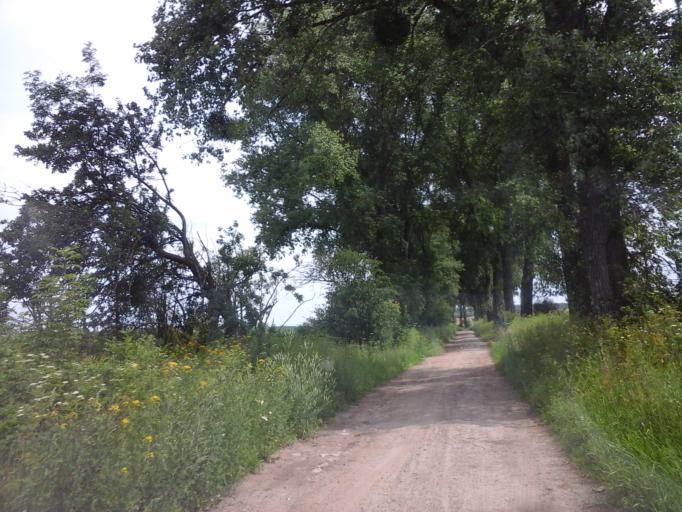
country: PL
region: West Pomeranian Voivodeship
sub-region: Powiat choszczenski
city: Recz
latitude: 53.2666
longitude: 15.6175
